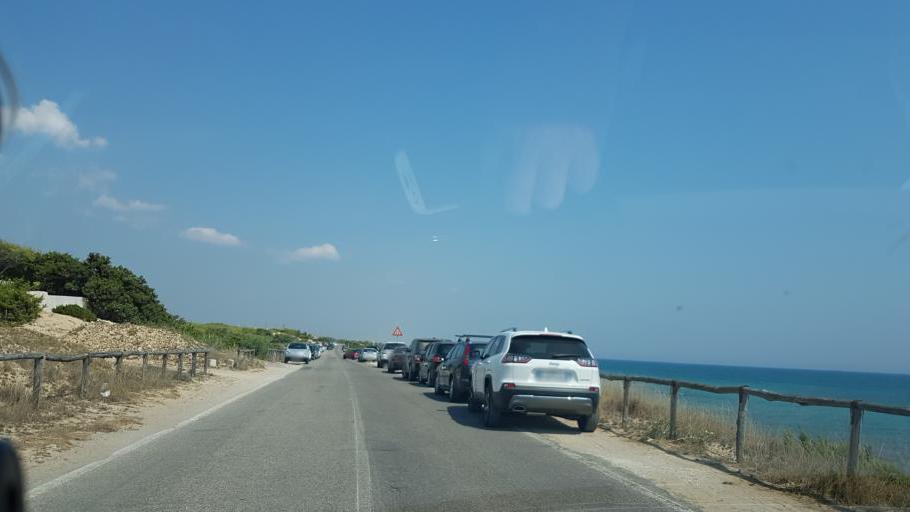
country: IT
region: Apulia
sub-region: Provincia di Taranto
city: Maruggio
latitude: 40.2993
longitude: 17.5918
